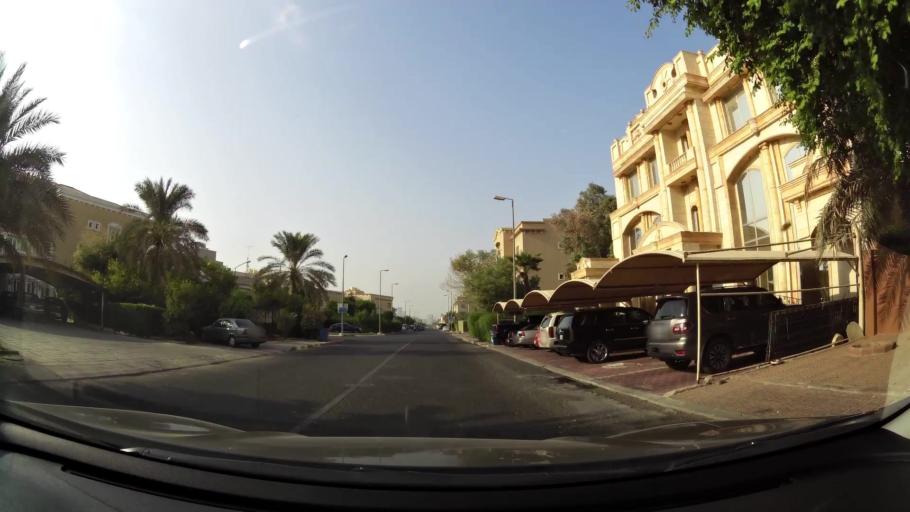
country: KW
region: Muhafazat Hawalli
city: Hawalli
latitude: 29.3263
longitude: 48.0073
